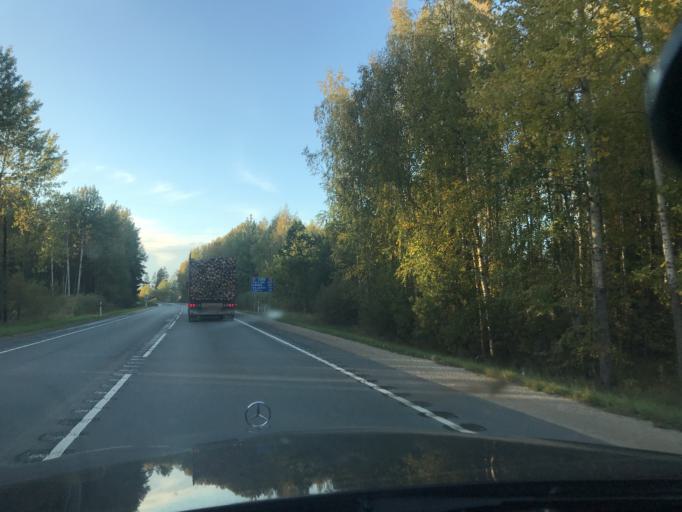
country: EE
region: Vorumaa
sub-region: Voru linn
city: Voru
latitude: 57.8622
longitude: 26.9669
